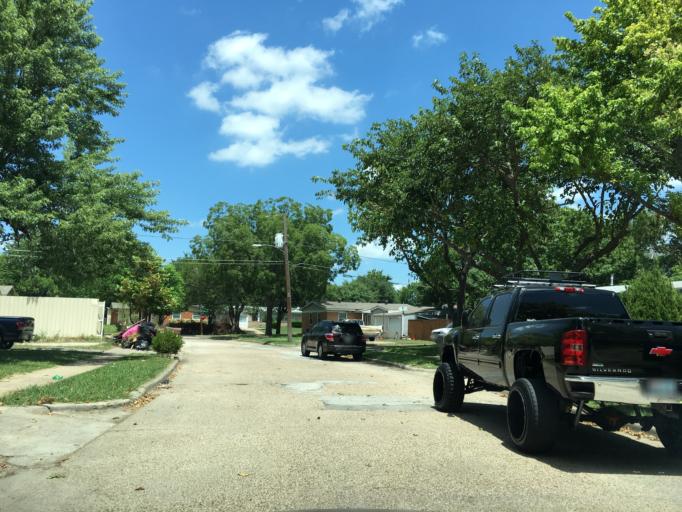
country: US
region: Texas
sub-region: Dallas County
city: Garland
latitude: 32.8355
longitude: -96.6608
